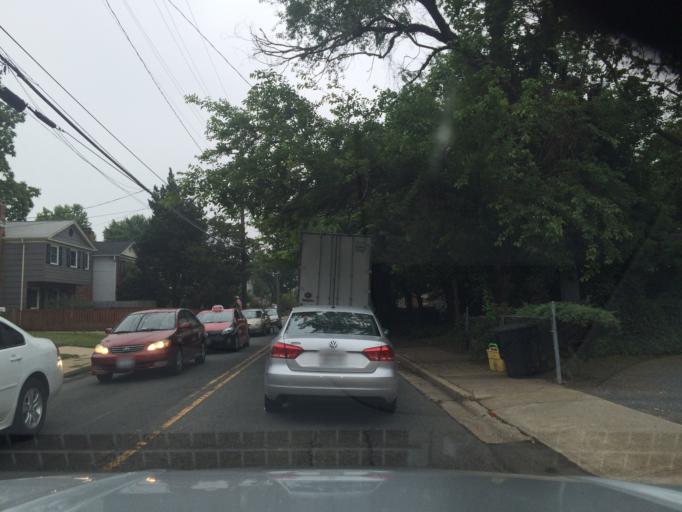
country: US
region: Virginia
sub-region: Arlington County
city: Arlington
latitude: 38.8707
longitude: -77.0883
